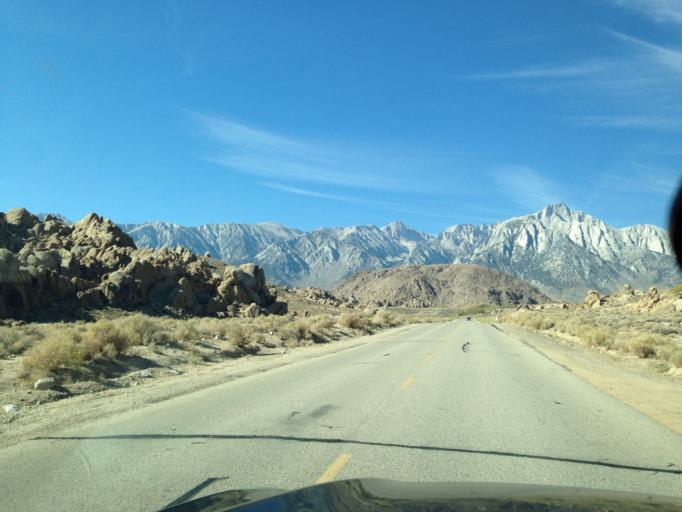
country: US
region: California
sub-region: Inyo County
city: Lone Pine
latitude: 36.5969
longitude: -118.0964
